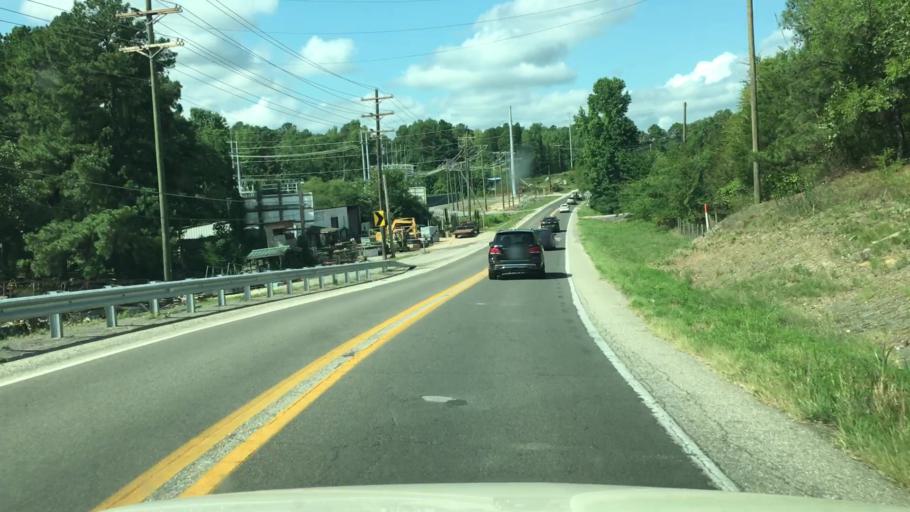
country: US
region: Arkansas
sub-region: Garland County
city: Lake Hamilton
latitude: 34.4046
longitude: -93.0912
